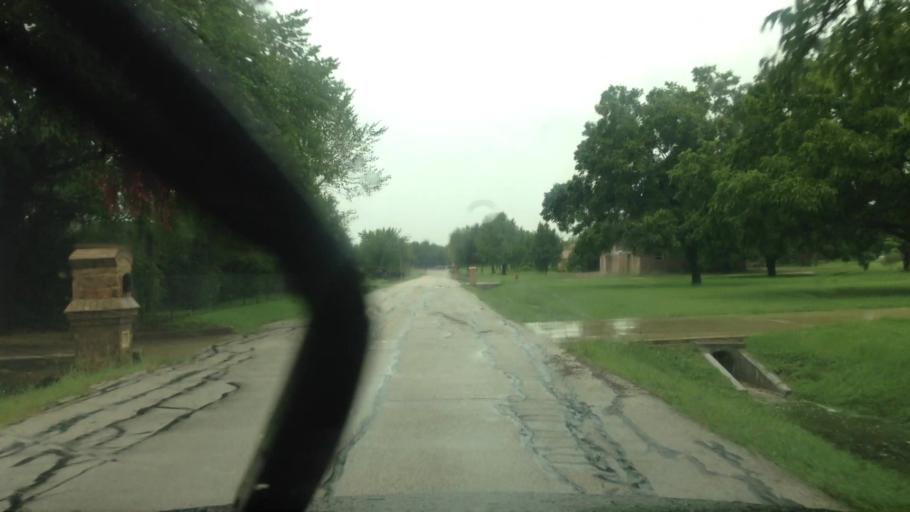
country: US
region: Texas
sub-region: Tarrant County
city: Watauga
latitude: 32.8719
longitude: -97.2254
